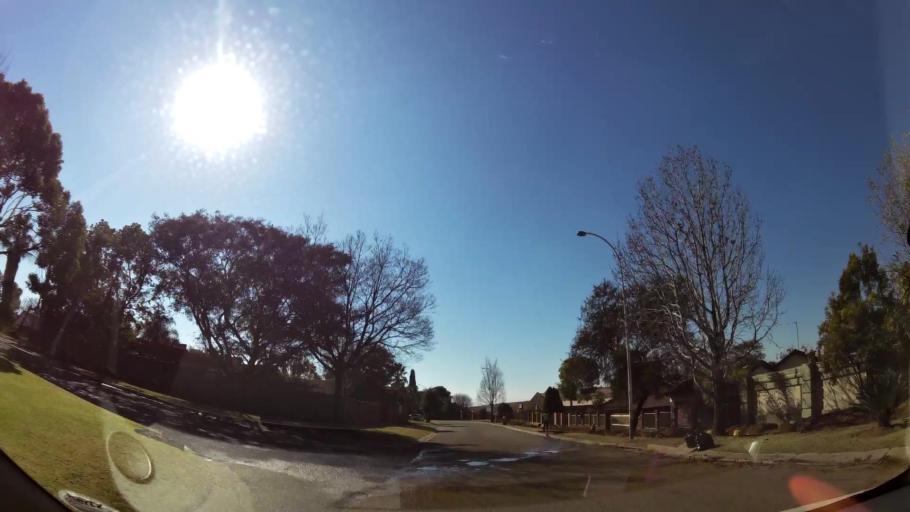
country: ZA
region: Mpumalanga
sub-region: Nkangala District Municipality
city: Witbank
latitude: -25.8759
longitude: 29.2519
